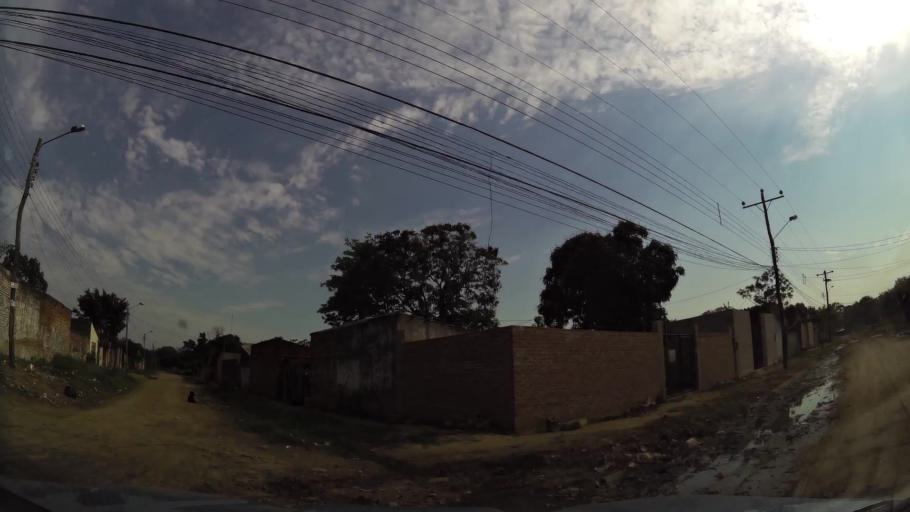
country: BO
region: Santa Cruz
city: Santa Cruz de la Sierra
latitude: -17.7202
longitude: -63.1359
